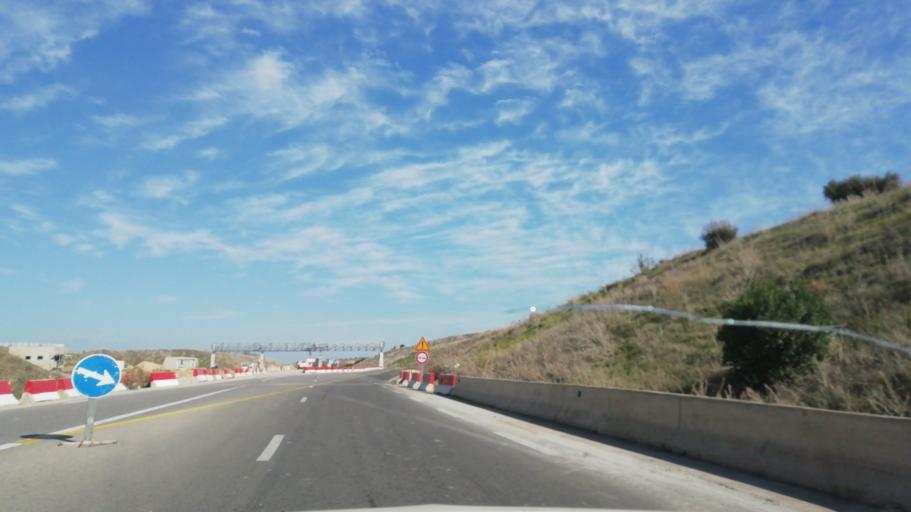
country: DZ
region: Tlemcen
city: Bensekrane
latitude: 34.9823
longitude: -1.2201
